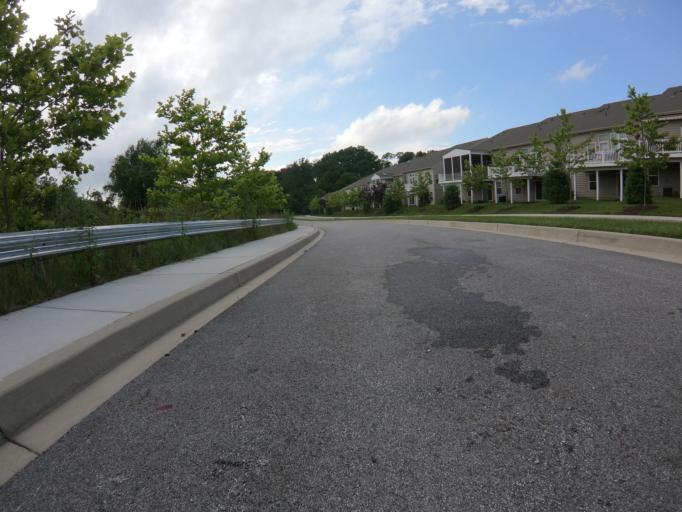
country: US
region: Maryland
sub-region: Howard County
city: Ellicott City
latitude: 39.2532
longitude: -76.7919
